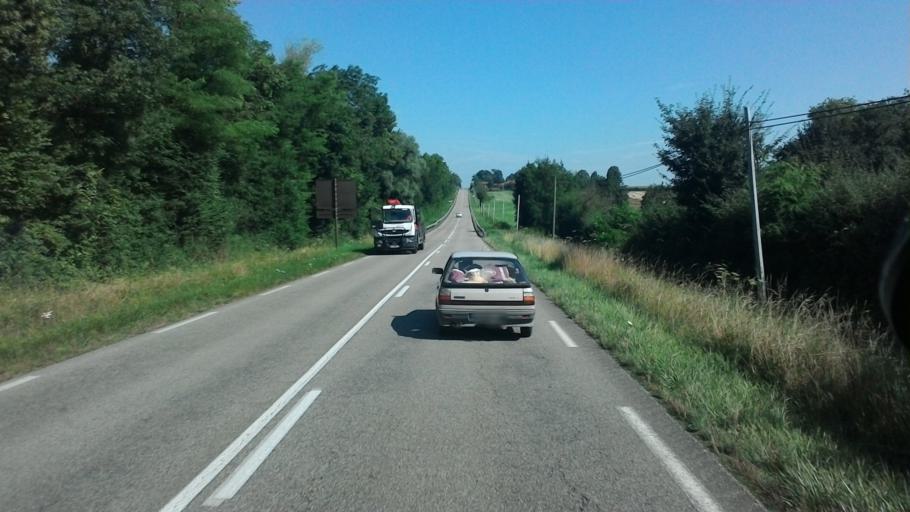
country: FR
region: Bourgogne
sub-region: Departement de Saone-et-Loire
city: Romenay
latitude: 46.4806
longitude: 5.0730
